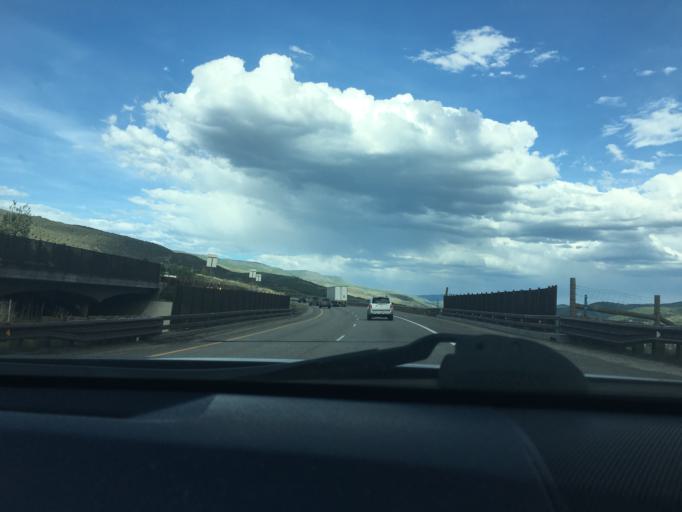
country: US
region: Colorado
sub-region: Eagle County
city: Edwards
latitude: 39.6560
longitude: -106.6289
